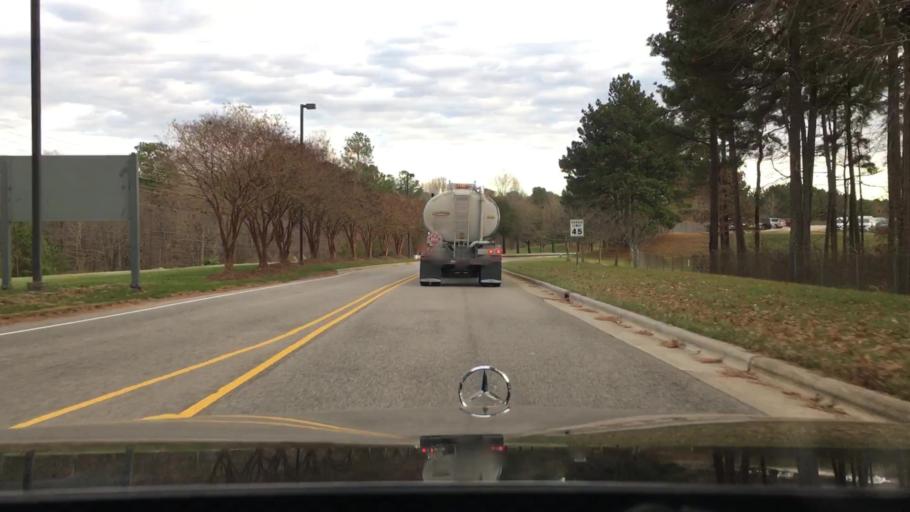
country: US
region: North Carolina
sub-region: Wake County
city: Morrisville
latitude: 35.8963
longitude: -78.7706
